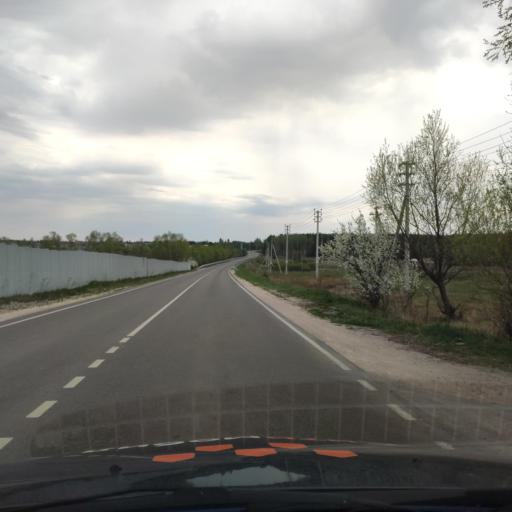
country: RU
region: Voronezj
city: Podgornoye
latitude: 51.8714
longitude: 39.1727
